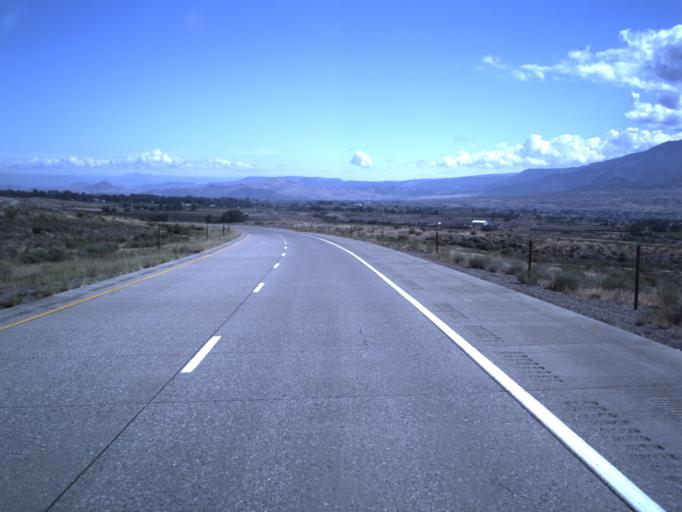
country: US
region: Utah
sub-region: Sevier County
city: Monroe
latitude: 38.6597
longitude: -112.1810
